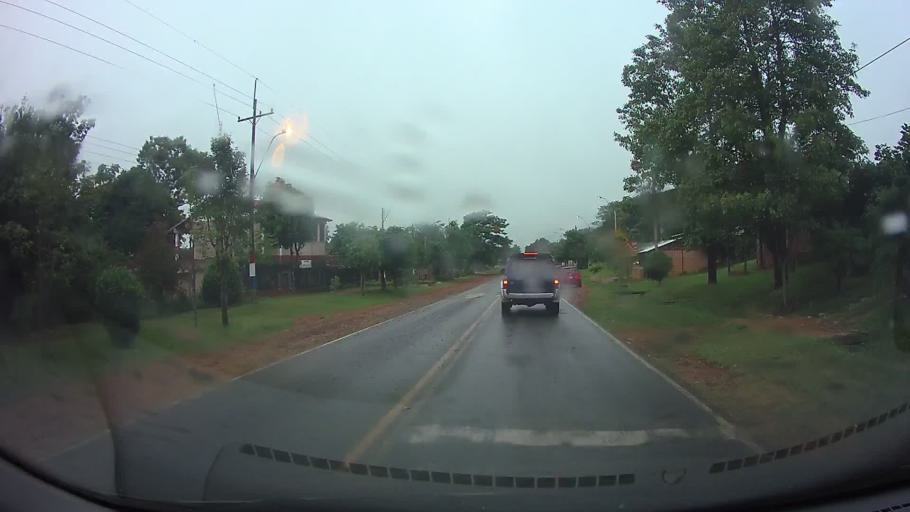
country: PY
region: Central
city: Ita
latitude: -25.4632
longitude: -57.3659
